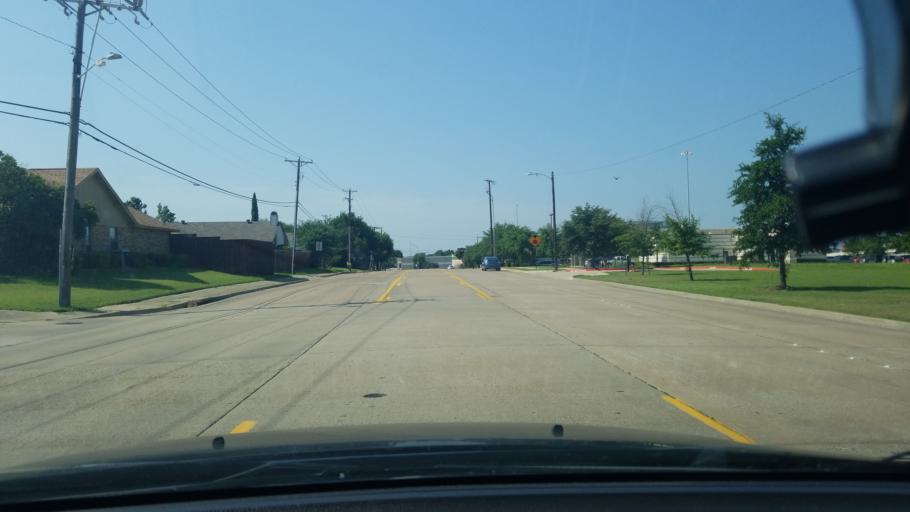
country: US
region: Texas
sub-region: Dallas County
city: Mesquite
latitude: 32.8185
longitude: -96.6271
